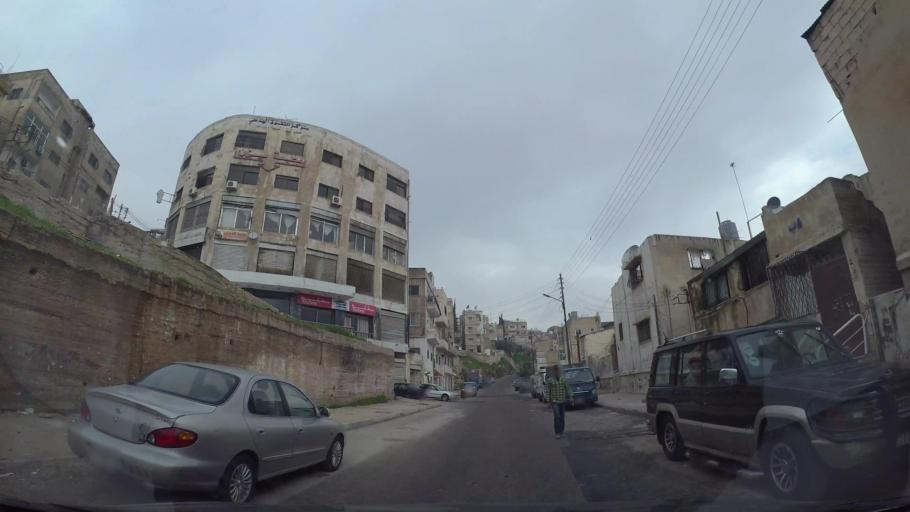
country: JO
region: Amman
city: Amman
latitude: 31.9646
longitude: 35.9297
